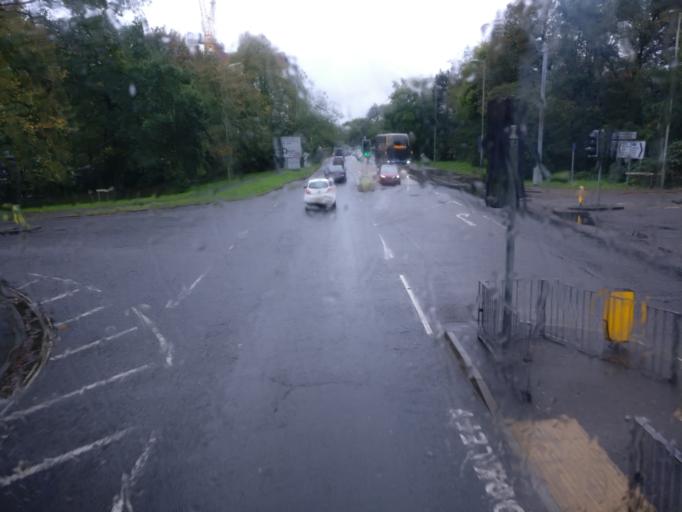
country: GB
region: England
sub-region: Hampshire
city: Farnborough
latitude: 51.2982
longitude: -0.7533
